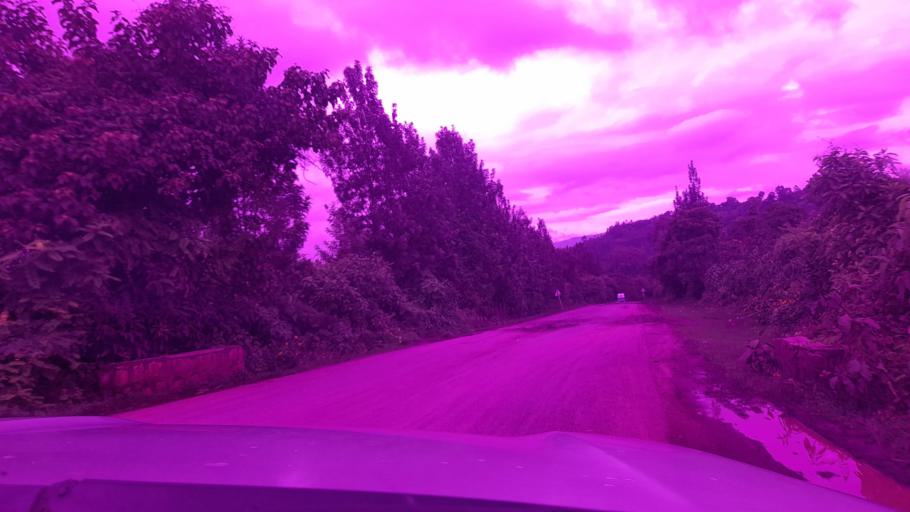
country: ET
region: Oromiya
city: Jima
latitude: 7.9213
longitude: 37.4049
